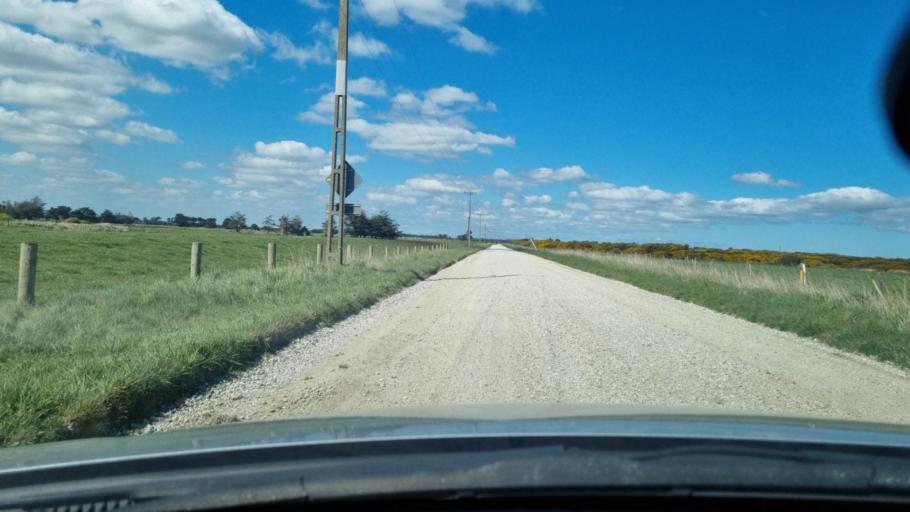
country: NZ
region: Southland
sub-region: Invercargill City
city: Invercargill
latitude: -46.3915
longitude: 168.2640
